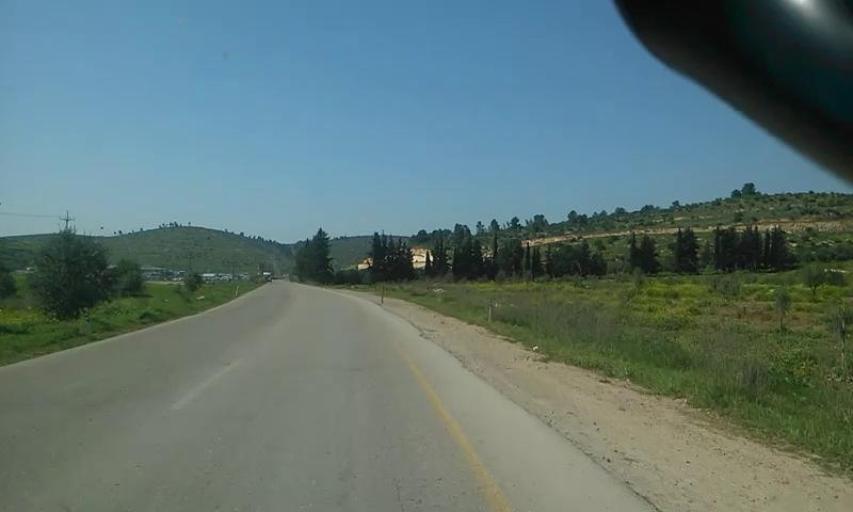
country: PS
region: West Bank
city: Idhna
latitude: 31.5892
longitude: 34.9690
